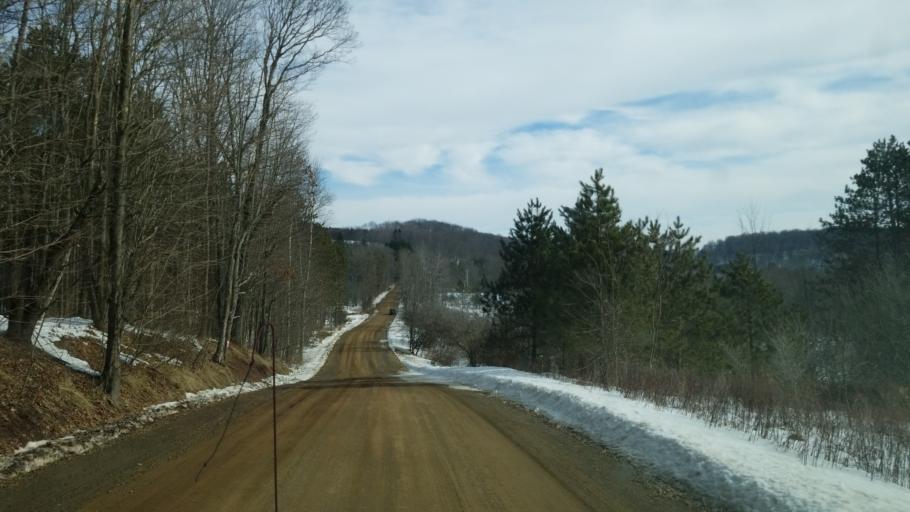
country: US
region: New York
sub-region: Allegany County
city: Andover
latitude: 42.0086
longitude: -77.8132
